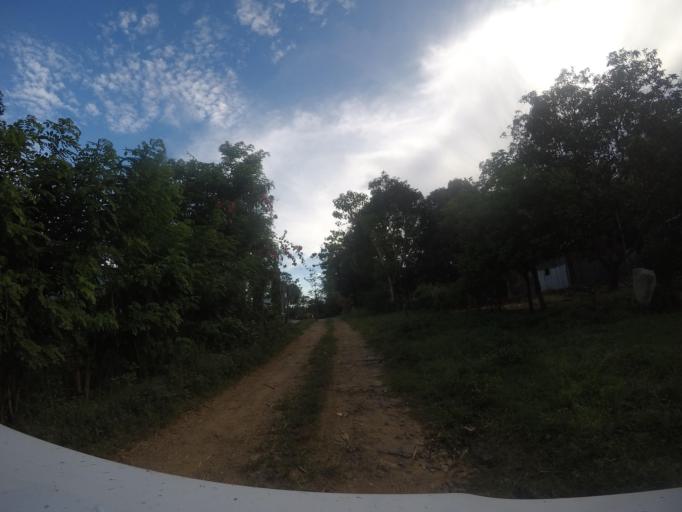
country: TL
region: Lautem
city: Lospalos
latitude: -8.5126
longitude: 126.9927
